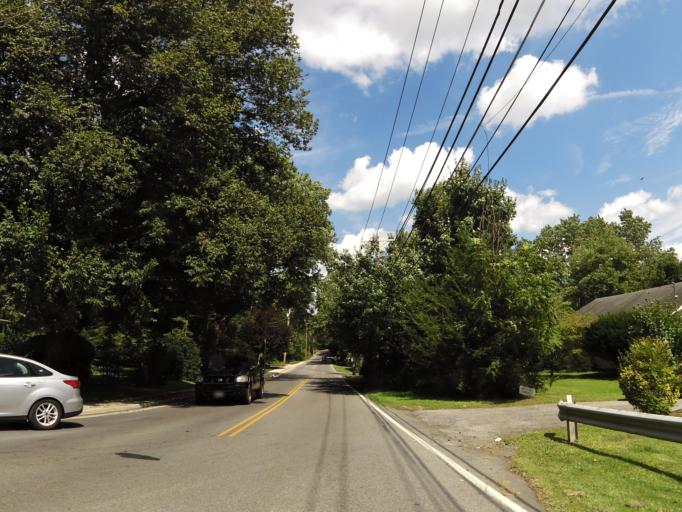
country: US
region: Virginia
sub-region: Washington County
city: Abingdon
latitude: 36.7148
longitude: -81.9661
